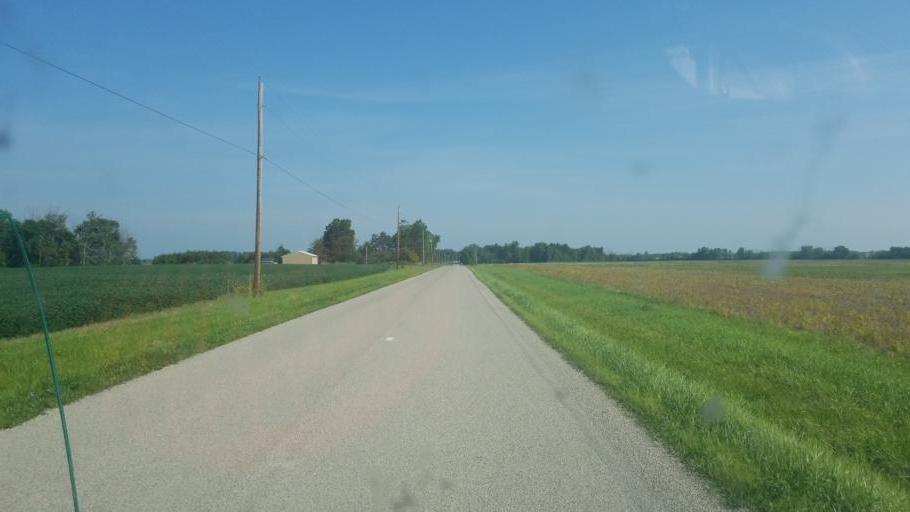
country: US
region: Ohio
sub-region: Lorain County
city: Wellington
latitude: 41.1233
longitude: -82.1802
